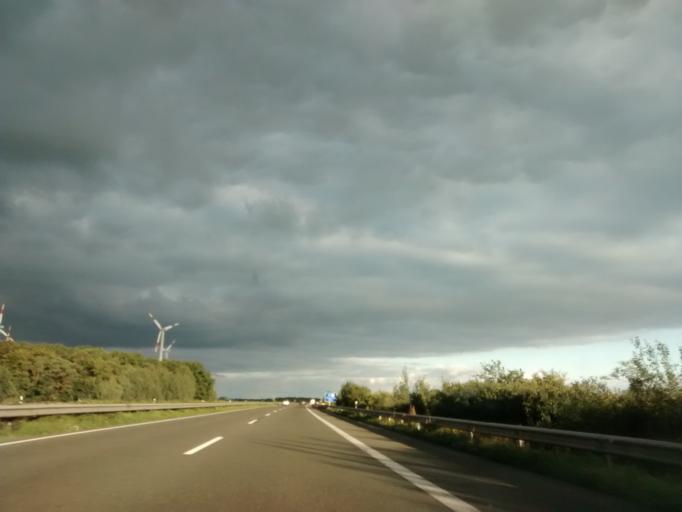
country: DE
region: Lower Saxony
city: Salzbergen
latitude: 52.3445
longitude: 7.3829
